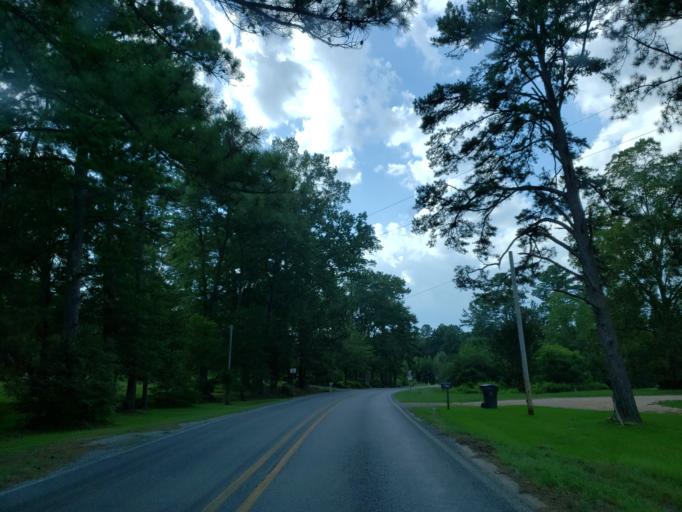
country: US
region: Mississippi
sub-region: Jones County
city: Sharon
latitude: 31.9109
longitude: -89.0178
